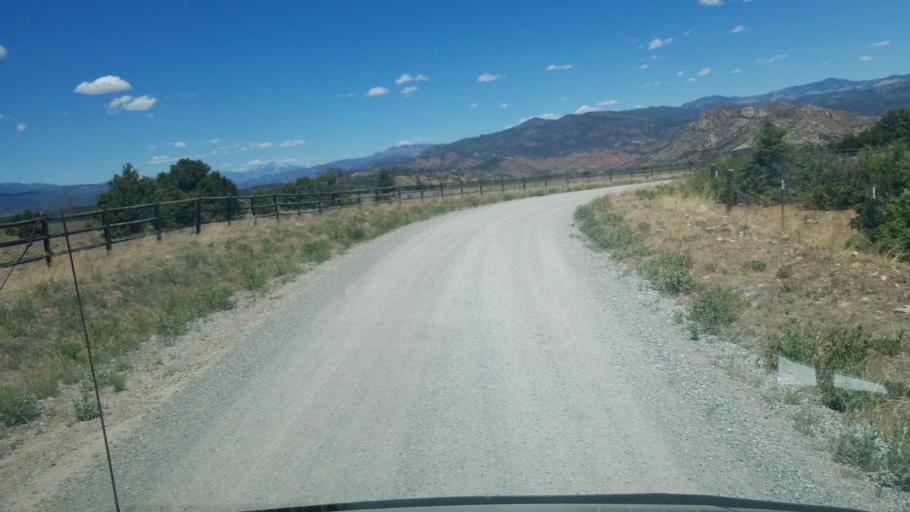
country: US
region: Colorado
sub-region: Custer County
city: Westcliffe
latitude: 38.3125
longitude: -105.6706
